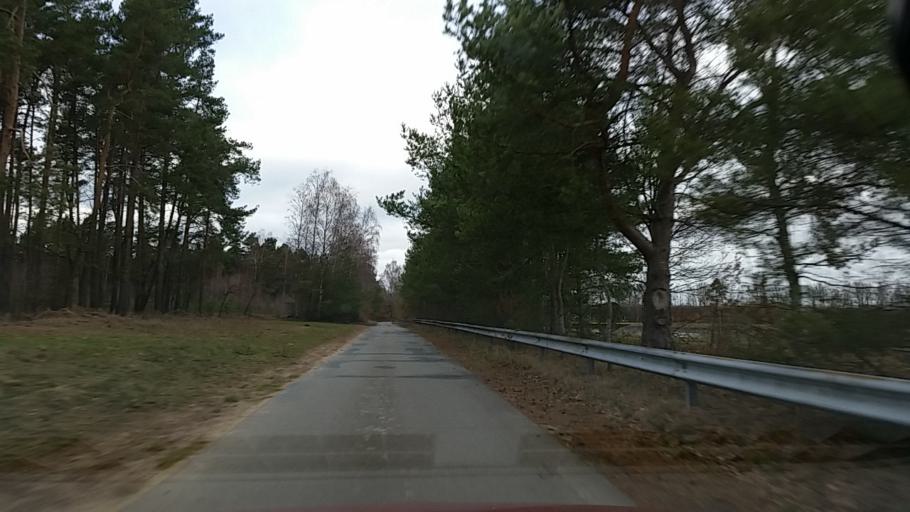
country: DE
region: Lower Saxony
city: Wieren
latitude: 52.8761
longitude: 10.6445
